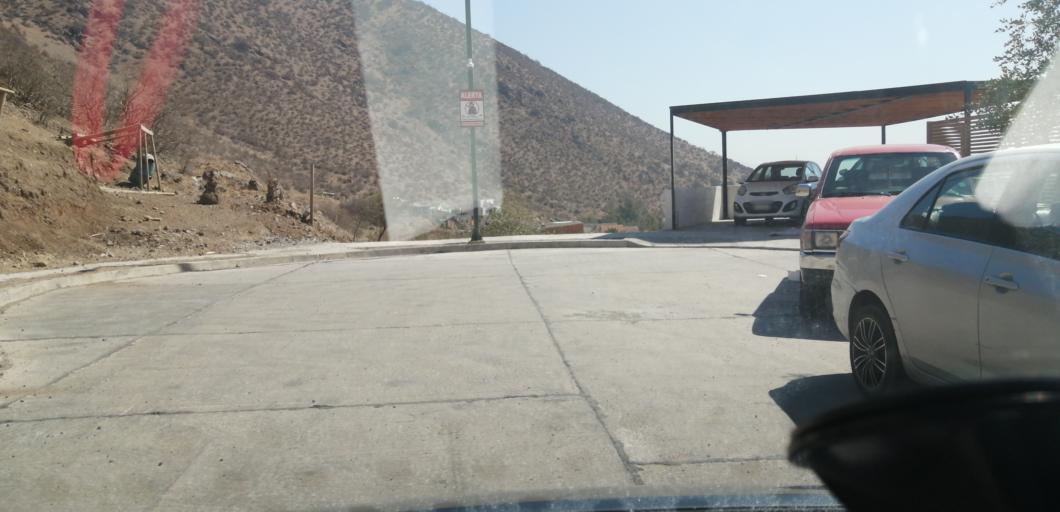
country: CL
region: Santiago Metropolitan
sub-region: Provincia de Santiago
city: Lo Prado
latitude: -33.4591
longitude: -70.8251
